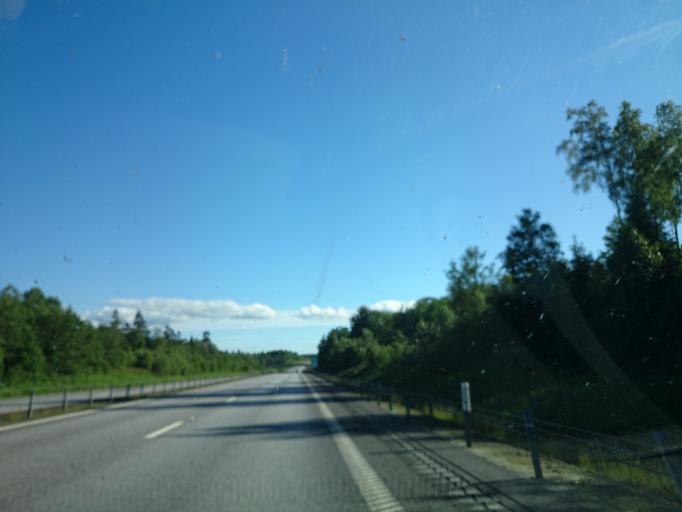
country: SE
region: Kronoberg
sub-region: Markaryds Kommun
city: Markaryd
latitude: 56.3483
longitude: 13.4653
